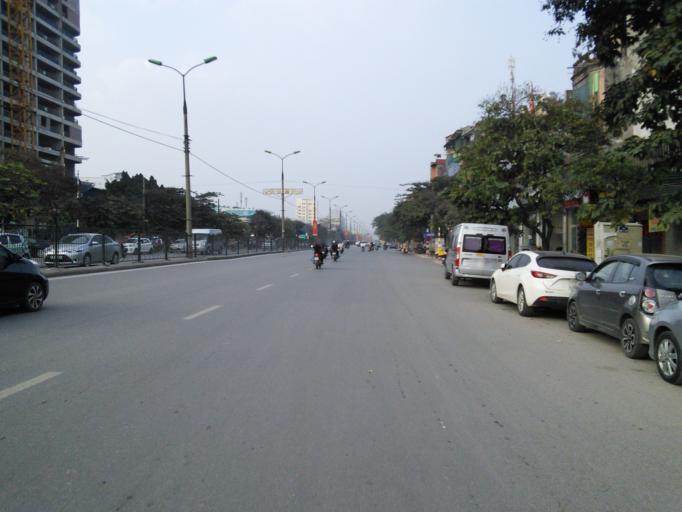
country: VN
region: Ha Noi
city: Hai BaTrung
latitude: 20.9852
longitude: 105.8411
